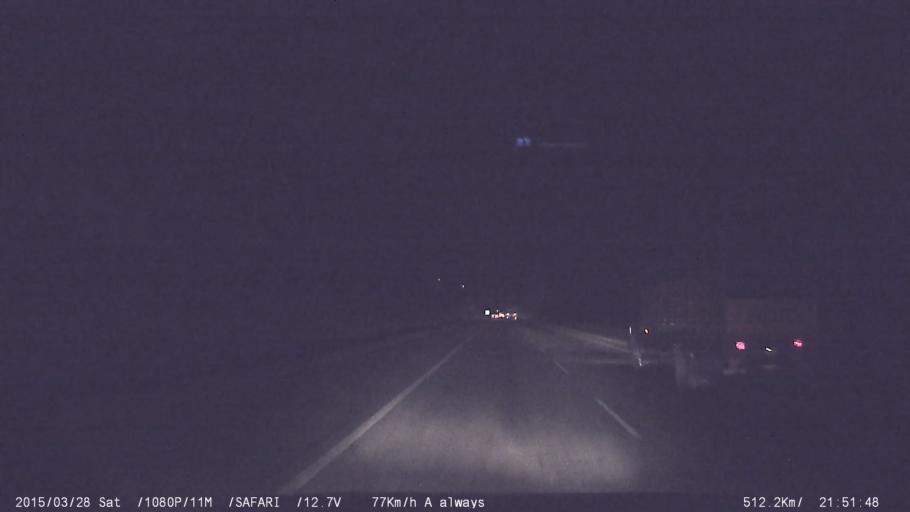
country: IN
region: Karnataka
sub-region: Bangalore Urban
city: Bangalore
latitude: 12.8558
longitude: 77.5343
